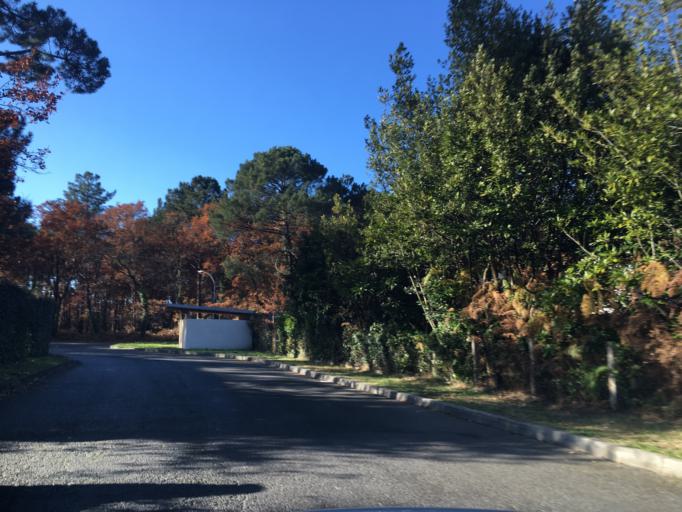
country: FR
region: Aquitaine
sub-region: Departement de la Gironde
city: La Teste-de-Buch
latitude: 44.6172
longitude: -1.1406
